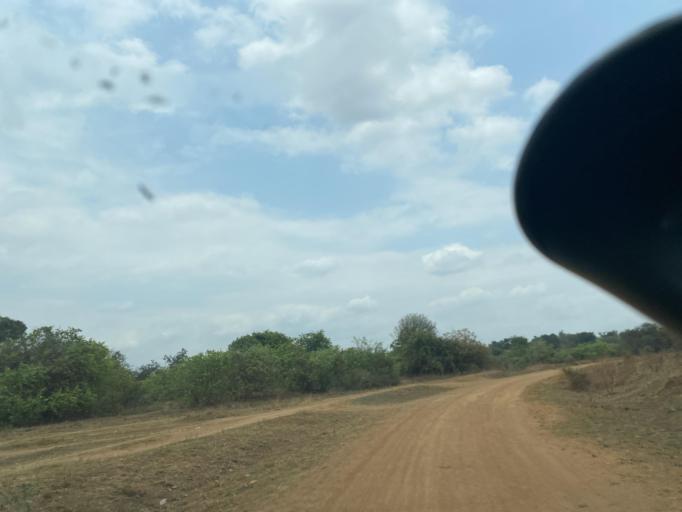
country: ZM
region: Lusaka
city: Chongwe
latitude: -15.5071
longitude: 28.8182
